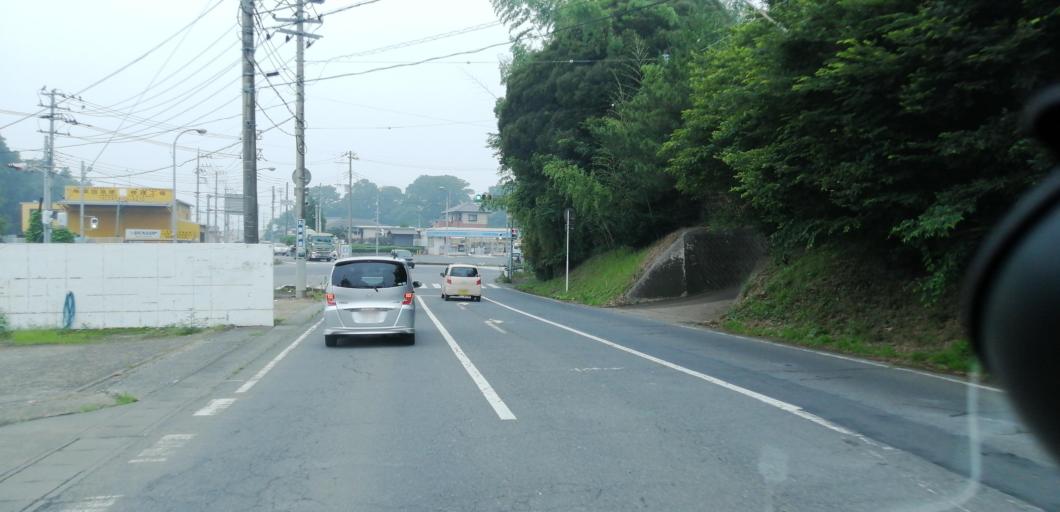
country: JP
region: Ibaraki
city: Iwai
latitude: 36.0319
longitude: 139.8369
